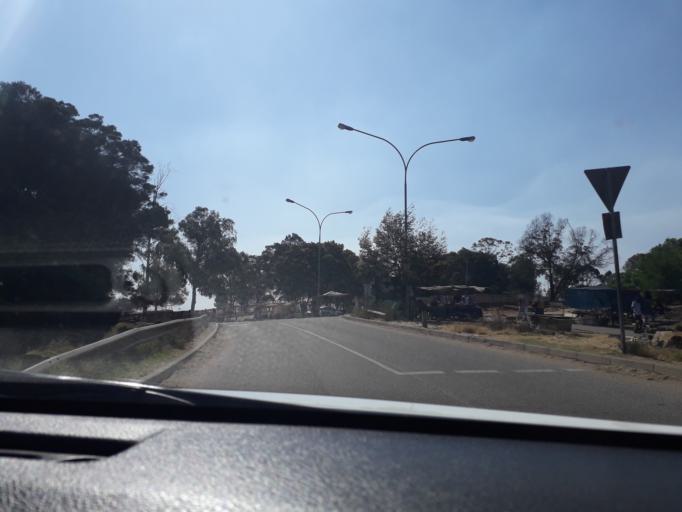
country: ZA
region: Gauteng
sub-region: City of Johannesburg Metropolitan Municipality
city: Modderfontein
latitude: -26.1082
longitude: 28.2262
